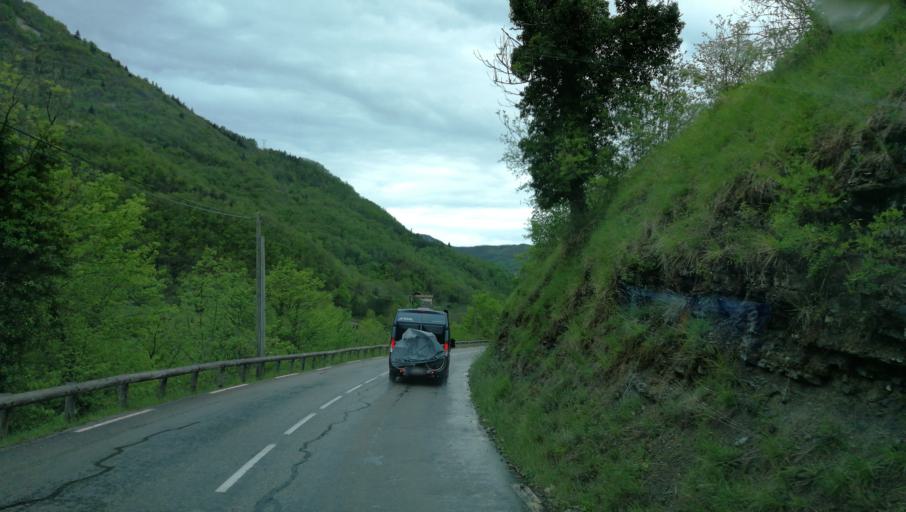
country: FR
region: Rhone-Alpes
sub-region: Departement de l'Isere
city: Pont-en-Royans
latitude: 45.0623
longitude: 5.4017
